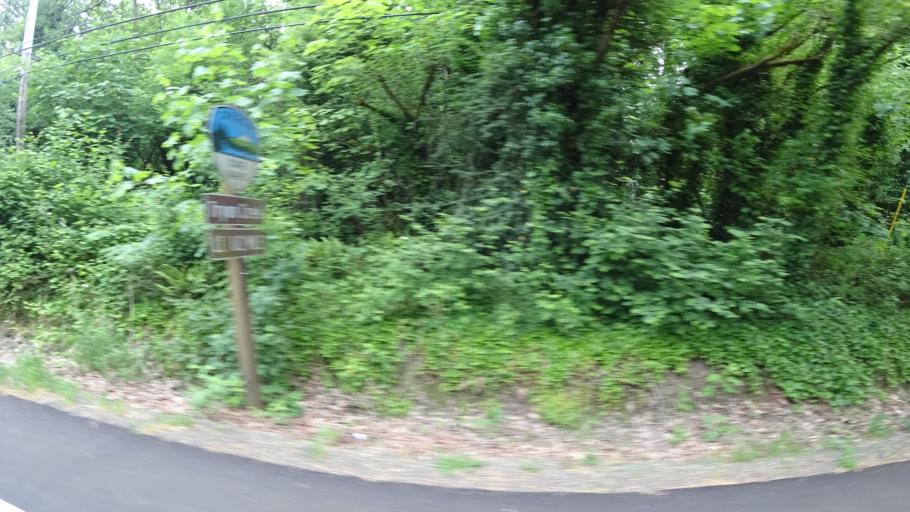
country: US
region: Oregon
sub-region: Clackamas County
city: Lake Oswego
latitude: 45.4366
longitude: -122.6679
